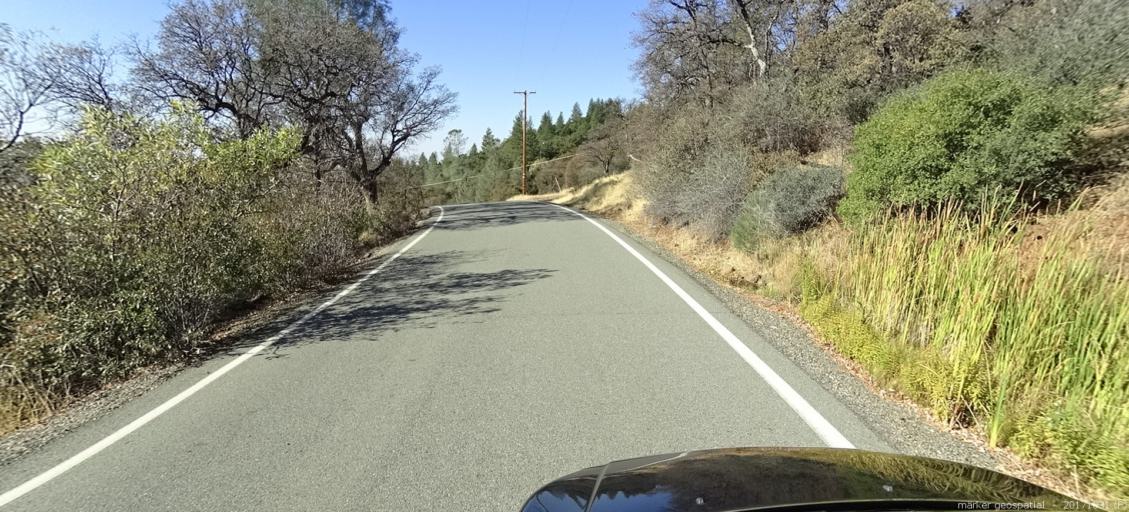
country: US
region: California
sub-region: Shasta County
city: Shingletown
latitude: 40.4656
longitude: -121.8850
